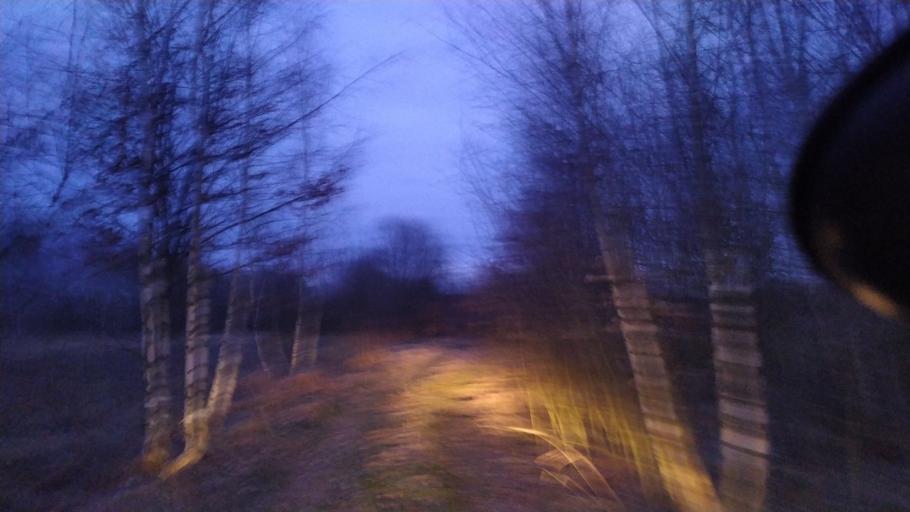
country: PL
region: Lublin Voivodeship
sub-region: Powiat lubelski
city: Jastkow
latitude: 51.3887
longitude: 22.4334
